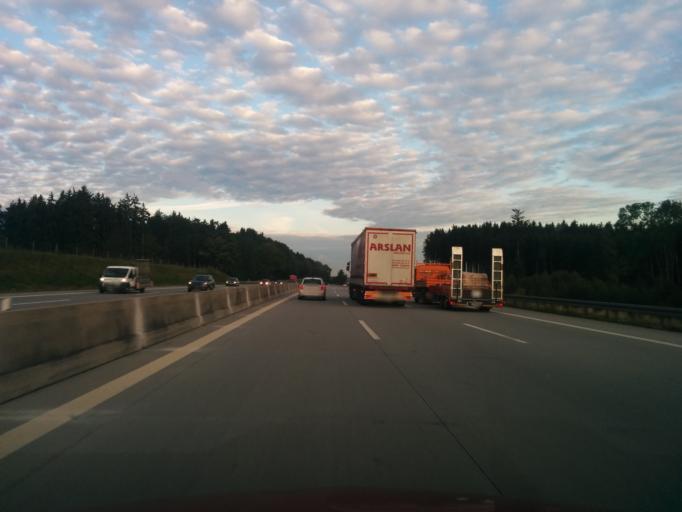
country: DE
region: Bavaria
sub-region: Swabia
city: Adelzhausen
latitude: 48.3676
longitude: 11.1108
